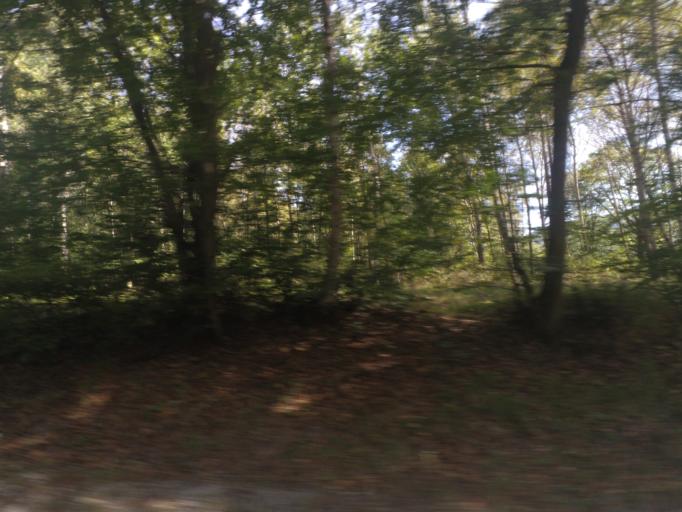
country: DE
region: Thuringia
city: Christes
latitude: 50.6457
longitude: 10.4655
